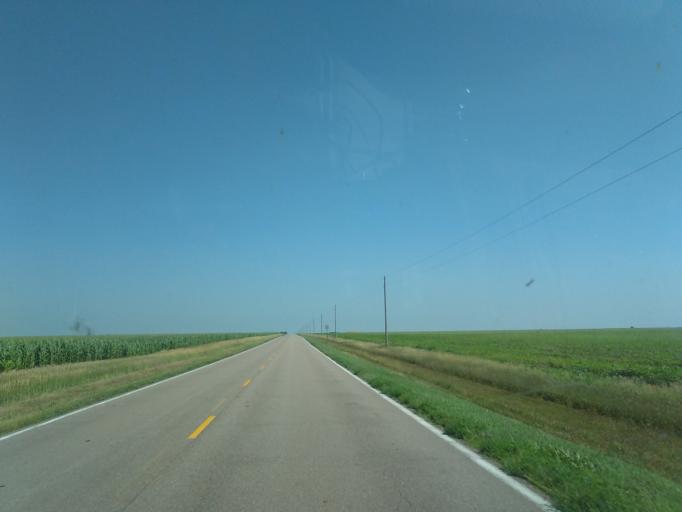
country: US
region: Nebraska
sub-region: Dundy County
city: Benkelman
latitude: 39.8304
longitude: -101.5410
